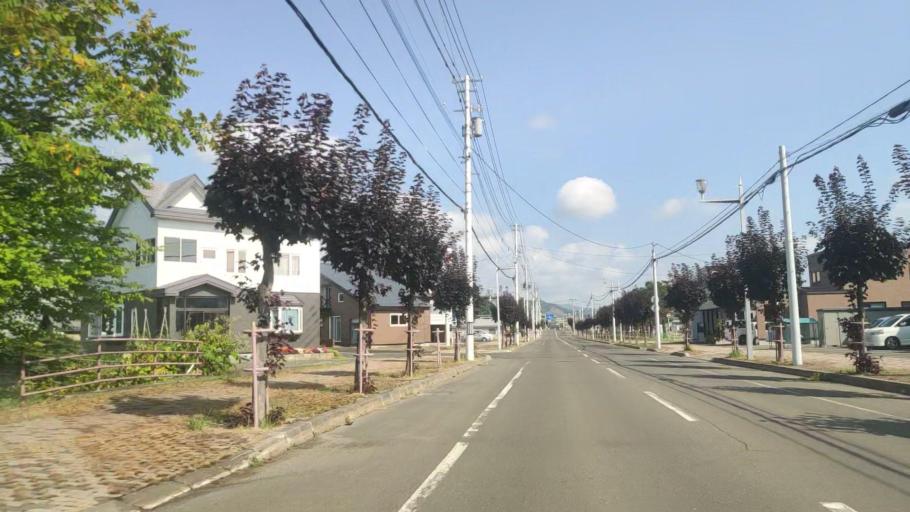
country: JP
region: Hokkaido
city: Shimo-furano
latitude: 43.3511
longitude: 142.3837
